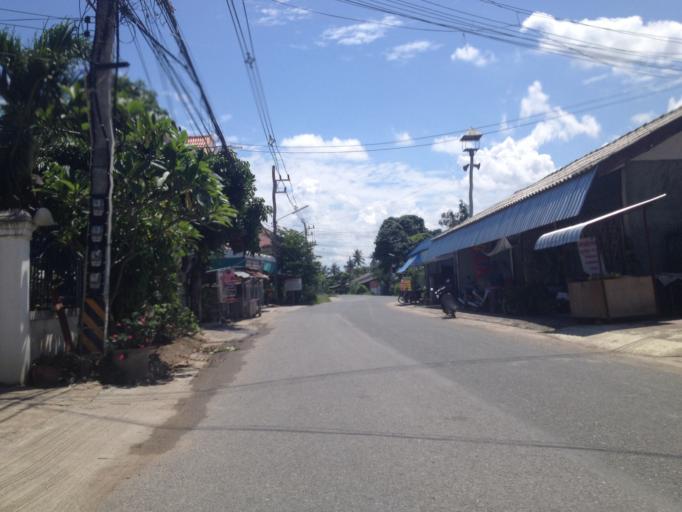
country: TH
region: Chiang Mai
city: Hang Dong
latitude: 18.6647
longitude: 98.9211
